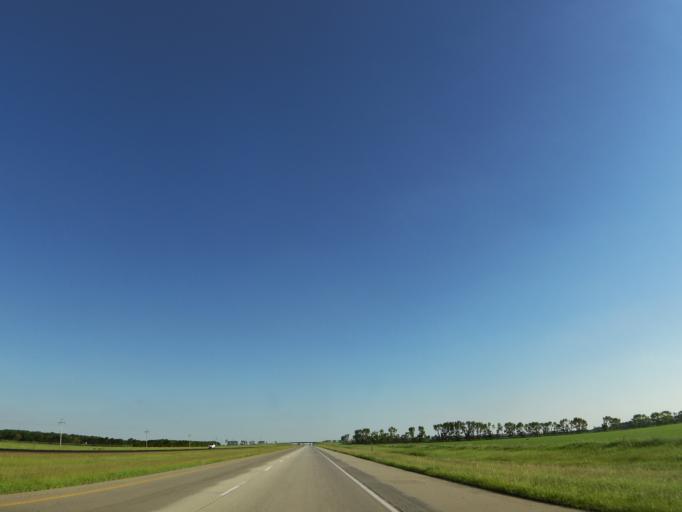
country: US
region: North Dakota
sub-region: Walsh County
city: Grafton
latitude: 48.2494
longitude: -97.1896
